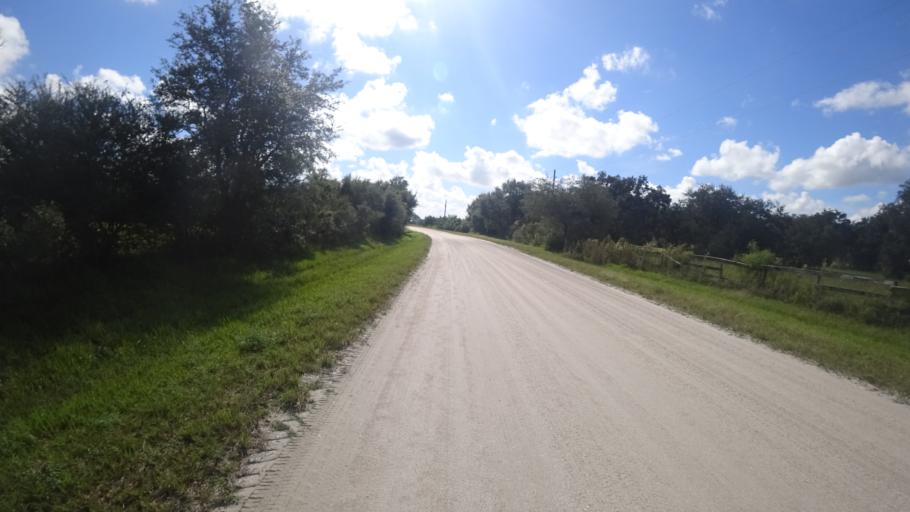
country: US
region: Florida
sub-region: DeSoto County
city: Arcadia
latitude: 27.3614
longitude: -82.1333
